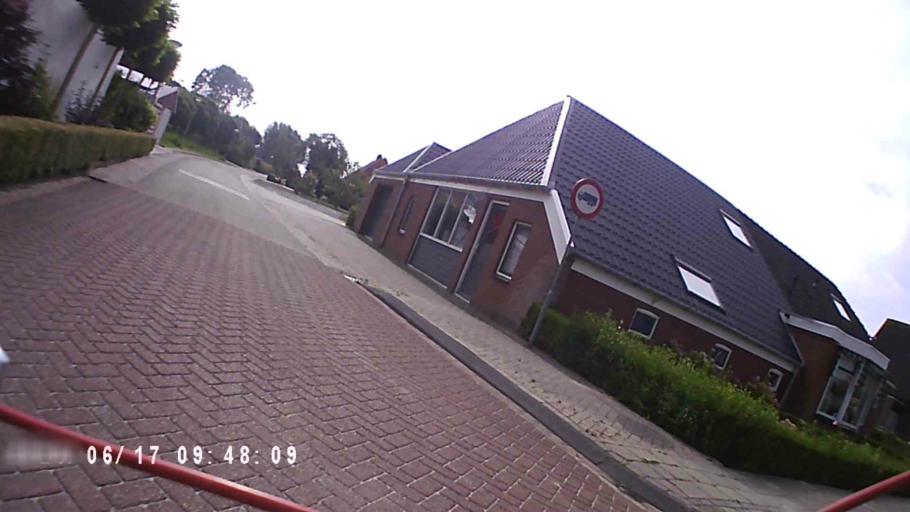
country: NL
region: Groningen
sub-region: Gemeente De Marne
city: Ulrum
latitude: 53.3583
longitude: 6.3382
